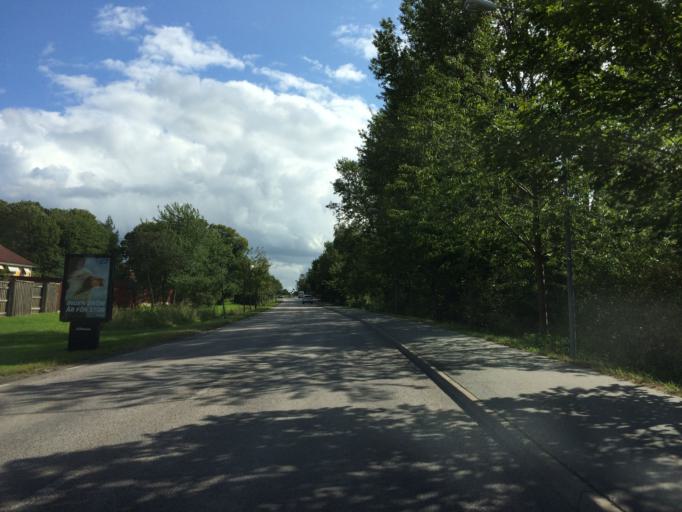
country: SE
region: Stockholm
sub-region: Sollentuna Kommun
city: Sollentuna
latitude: 59.4316
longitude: 17.9320
